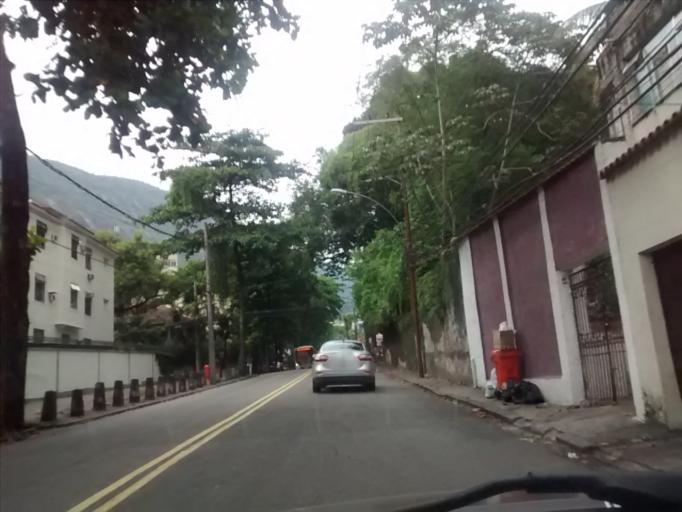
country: BR
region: Rio de Janeiro
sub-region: Rio De Janeiro
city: Rio de Janeiro
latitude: -22.9430
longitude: -43.2548
